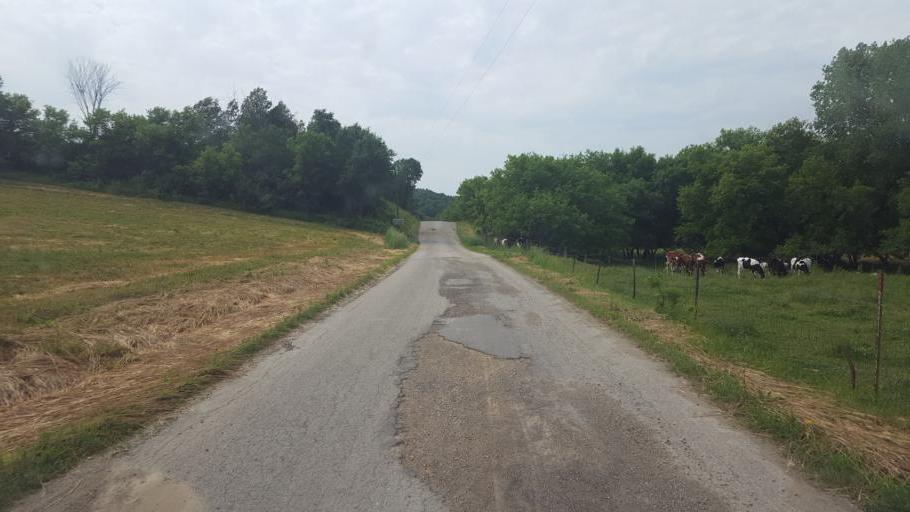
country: US
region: Wisconsin
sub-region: Monroe County
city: Cashton
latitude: 43.7264
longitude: -90.6521
